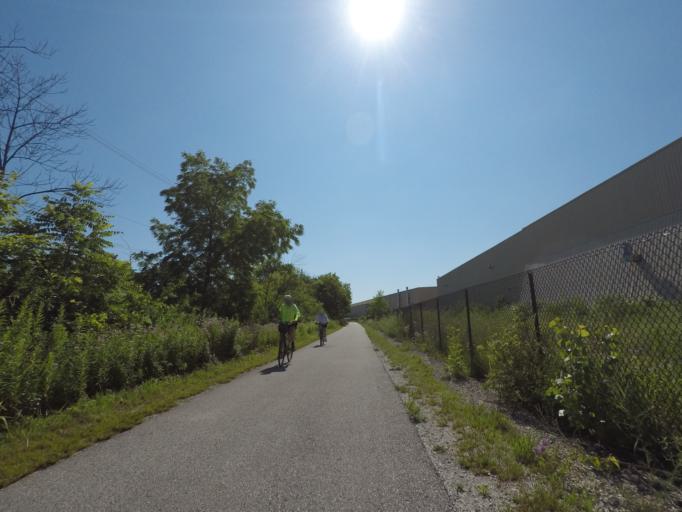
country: US
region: Wisconsin
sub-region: Milwaukee County
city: West Milwaukee
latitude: 43.0244
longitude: -87.9673
